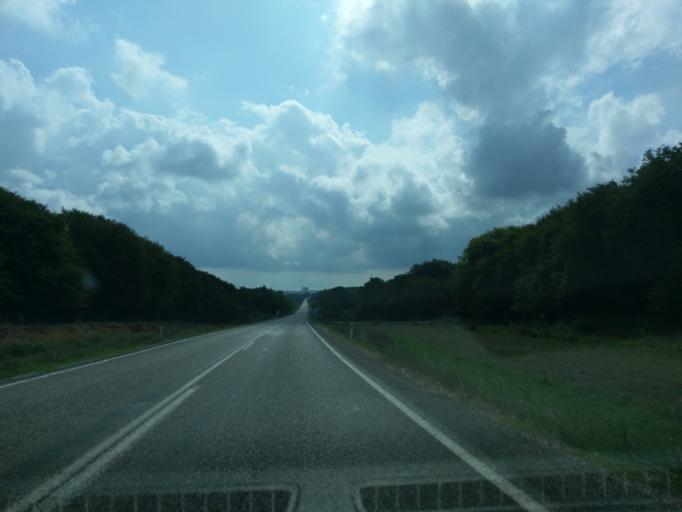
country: TR
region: Sinop
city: Sinop
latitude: 42.0301
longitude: 35.0322
